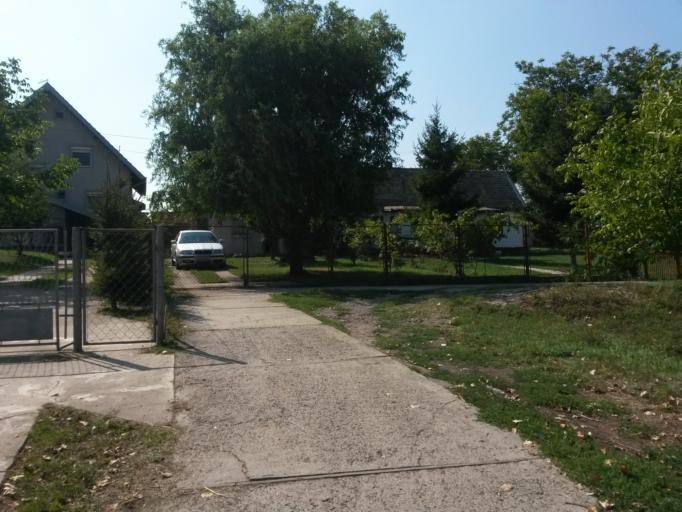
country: HR
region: Osjecko-Baranjska
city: Brijest
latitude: 45.5441
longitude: 18.6678
